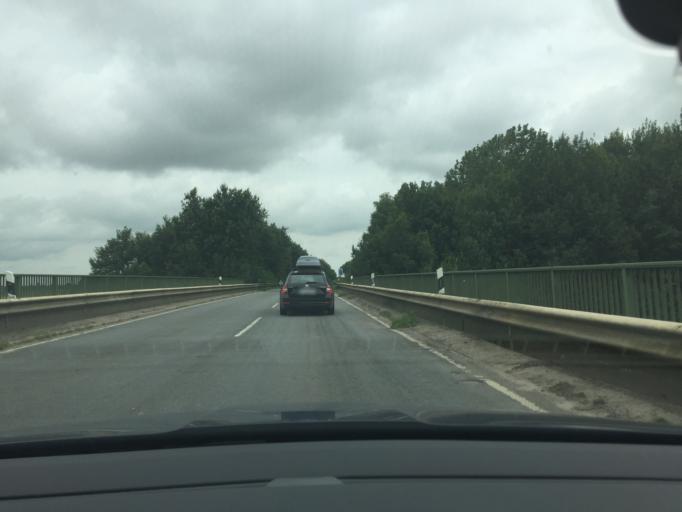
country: DE
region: Lower Saxony
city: Jemgum
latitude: 53.3672
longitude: 7.3477
